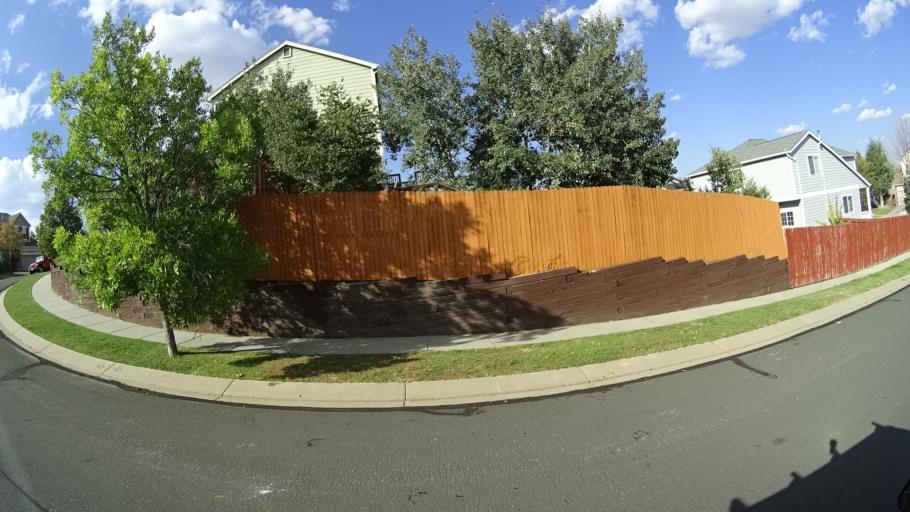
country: US
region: Colorado
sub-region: El Paso County
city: Cimarron Hills
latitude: 38.9102
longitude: -104.7274
